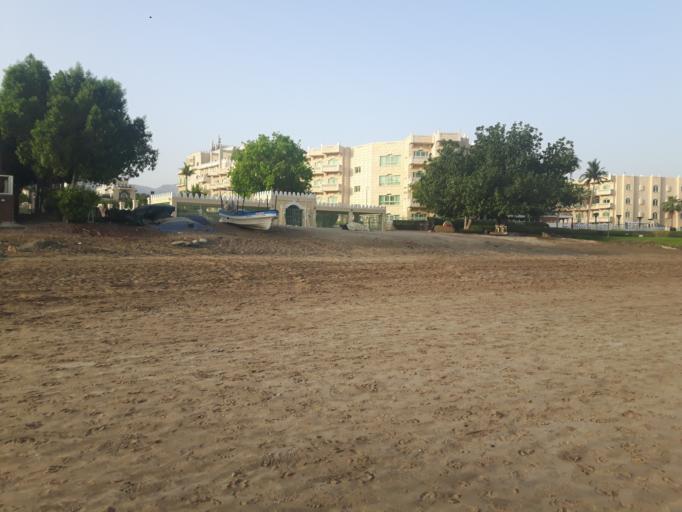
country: OM
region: Muhafazat Masqat
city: Bawshar
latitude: 23.6105
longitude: 58.4450
